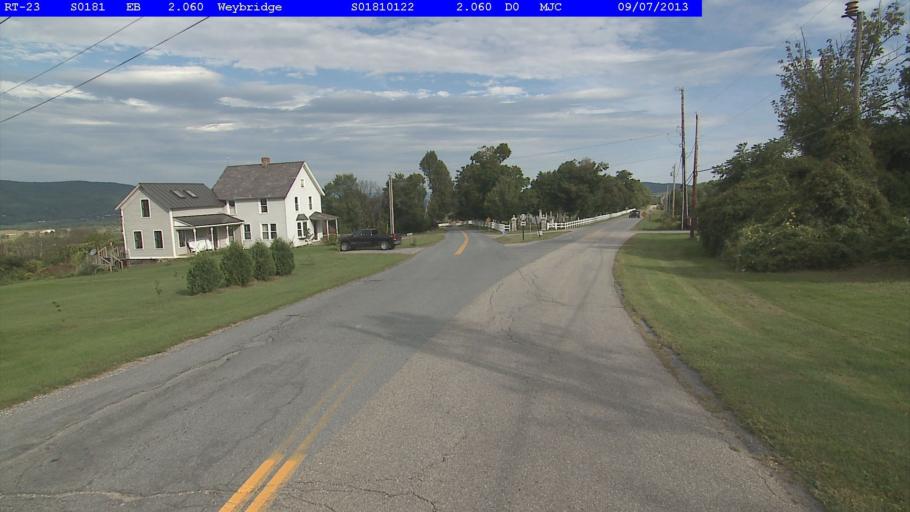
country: US
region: Vermont
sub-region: Addison County
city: Middlebury (village)
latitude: 44.0387
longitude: -73.2126
